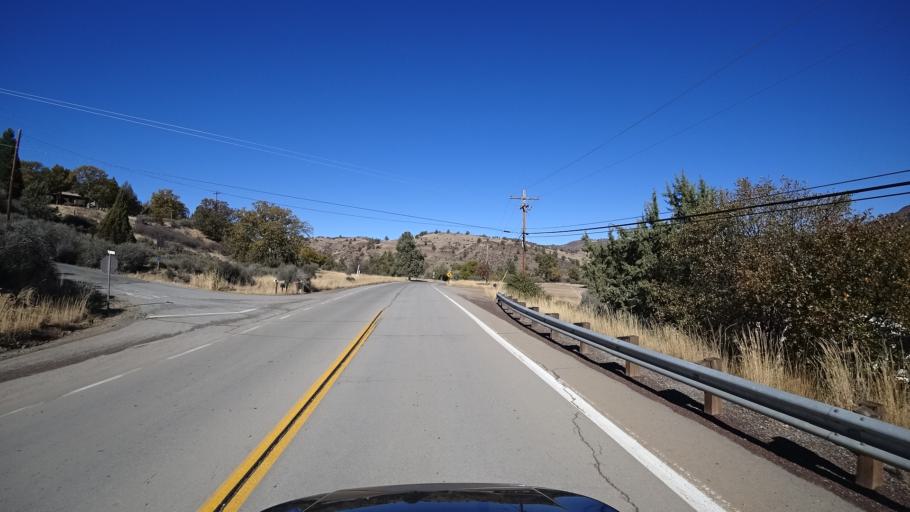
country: US
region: California
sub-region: Siskiyou County
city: Montague
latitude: 41.8968
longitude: -122.5076
